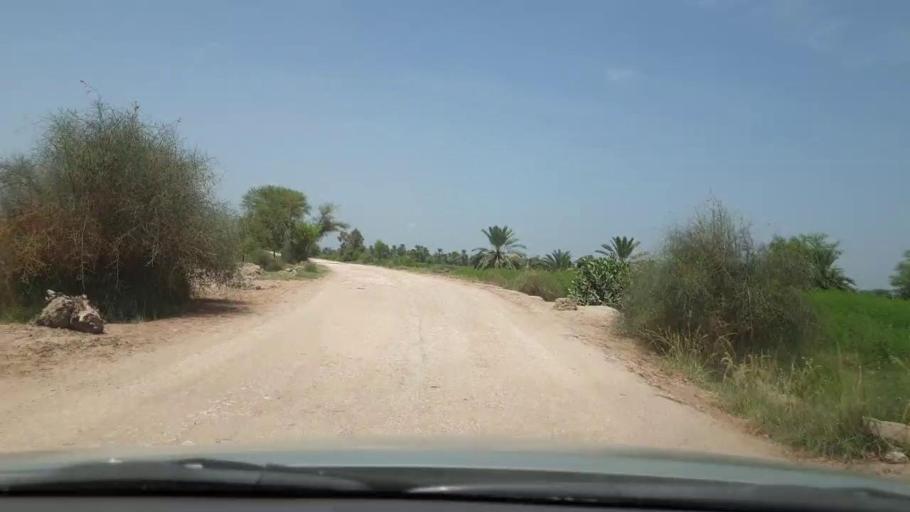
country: PK
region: Sindh
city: Pano Aqil
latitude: 27.7027
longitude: 69.2180
